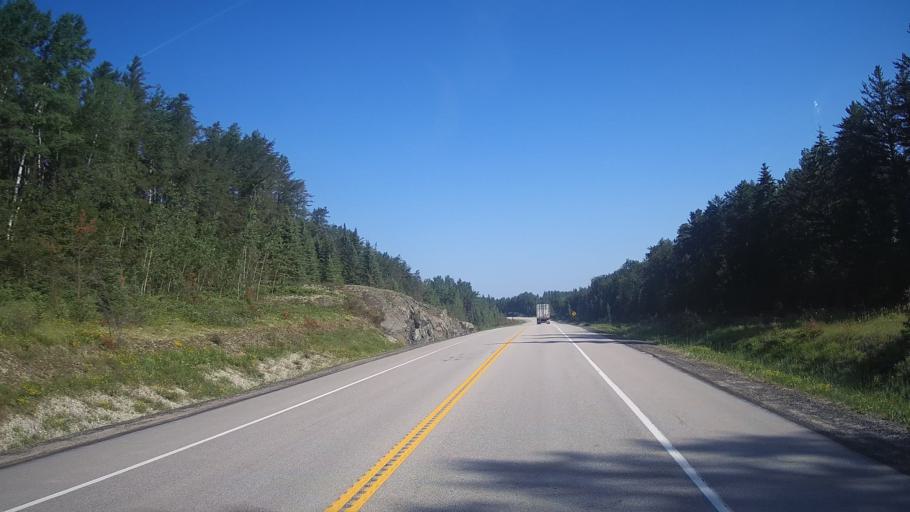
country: CA
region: Ontario
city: Dryden
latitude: 49.5784
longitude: -92.2616
